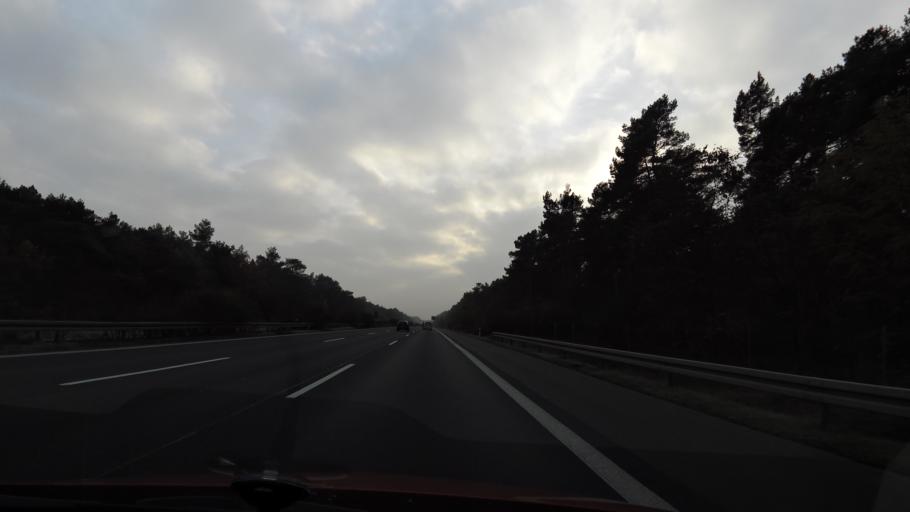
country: DE
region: Brandenburg
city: Fichtenwalde
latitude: 52.2263
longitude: 12.9109
